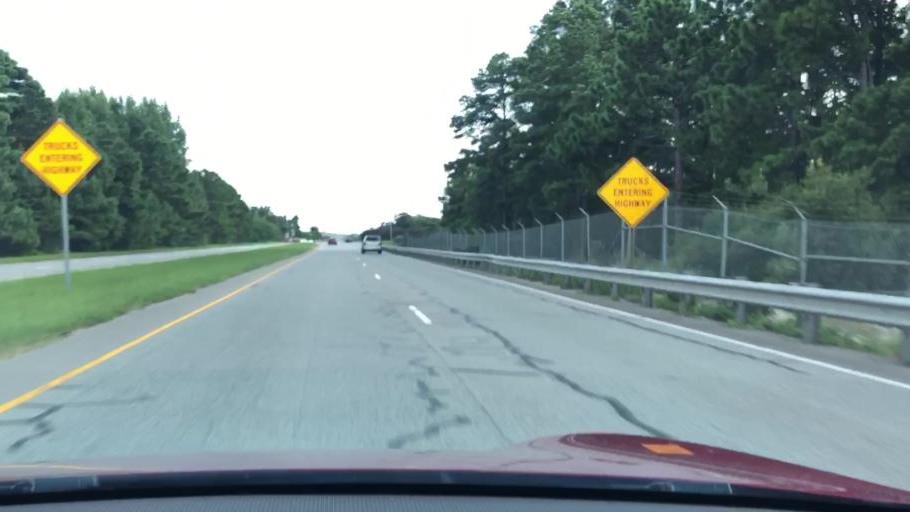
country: US
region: Virginia
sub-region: City of Virginia Beach
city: Virginia Beach
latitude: 36.8305
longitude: -76.0112
